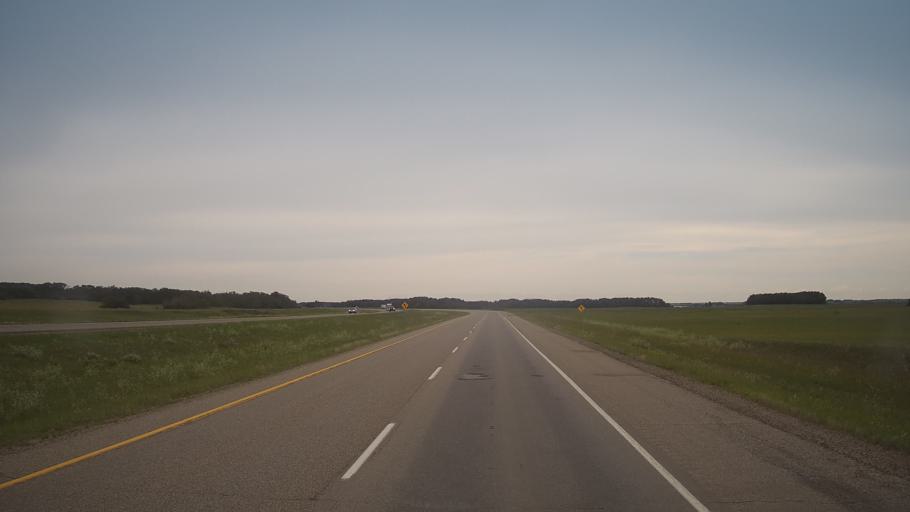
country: CA
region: Saskatchewan
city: Saskatoon
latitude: 51.8640
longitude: -106.5066
